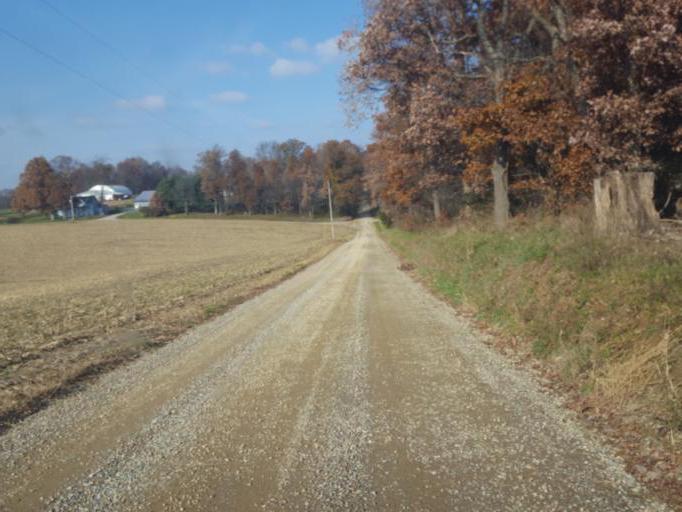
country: US
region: Ohio
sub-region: Knox County
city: Danville
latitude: 40.4129
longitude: -82.2920
